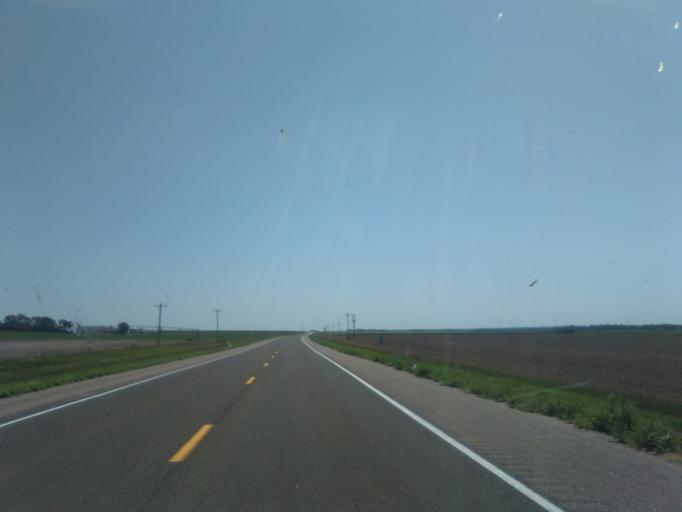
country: US
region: Nebraska
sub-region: Dundy County
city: Benkelman
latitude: 40.1257
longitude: -101.3512
